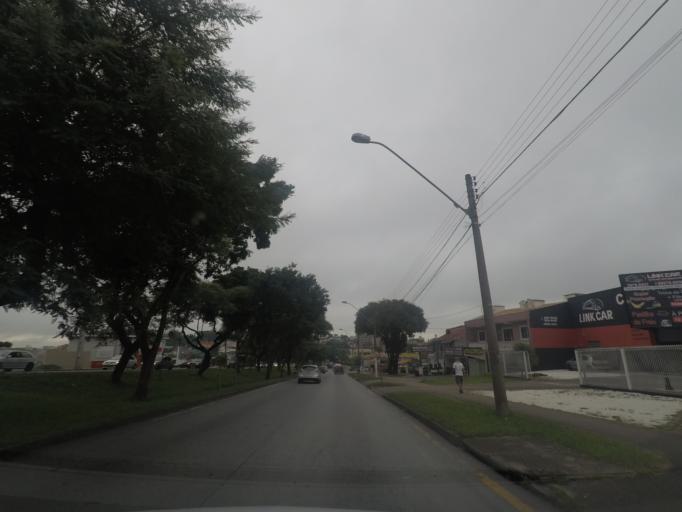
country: BR
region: Parana
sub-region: Pinhais
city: Pinhais
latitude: -25.3809
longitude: -49.2193
